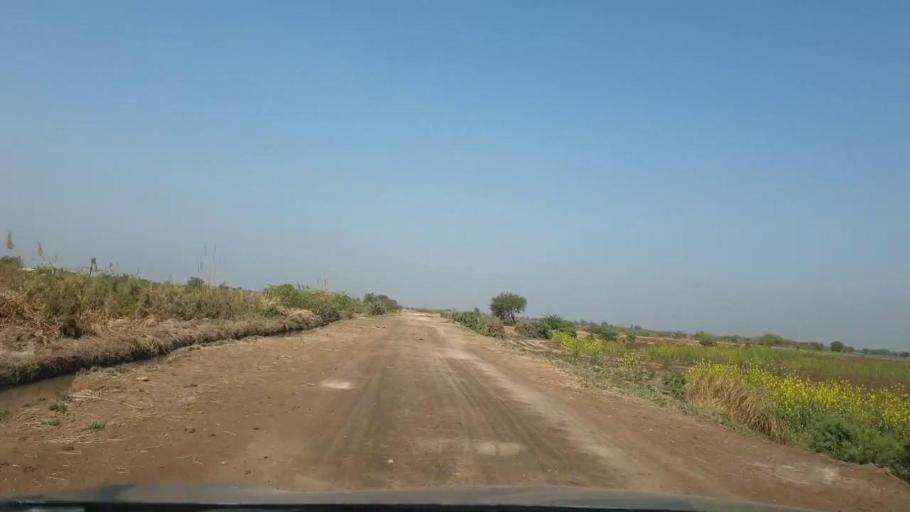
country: PK
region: Sindh
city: Berani
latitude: 25.7104
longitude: 68.8611
